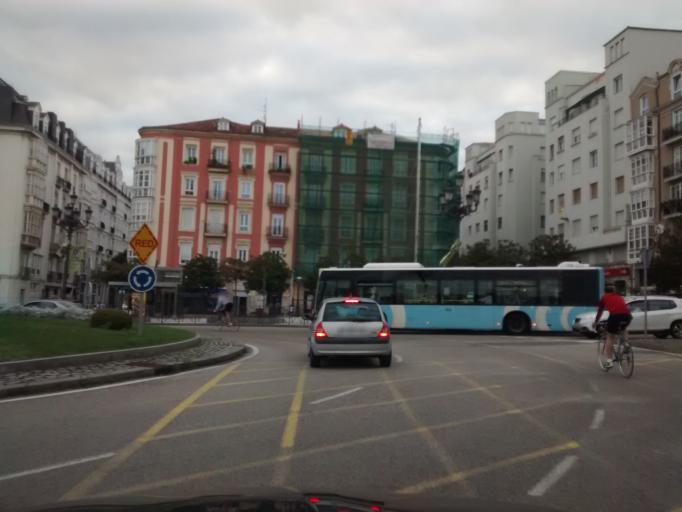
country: ES
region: Cantabria
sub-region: Provincia de Cantabria
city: Santander
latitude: 43.4631
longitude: -3.7963
